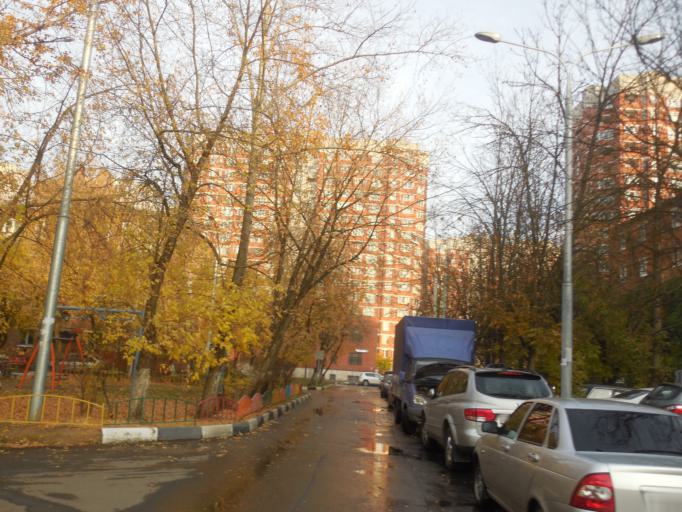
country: RU
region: Moskovskaya
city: Shcherbinka
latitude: 55.5008
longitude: 37.5668
